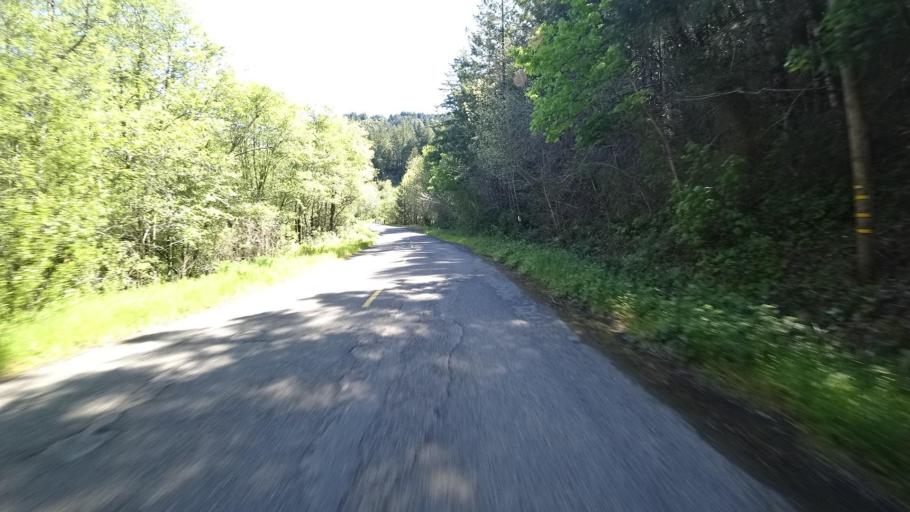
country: US
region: California
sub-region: Humboldt County
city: Rio Dell
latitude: 40.2297
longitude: -124.1438
